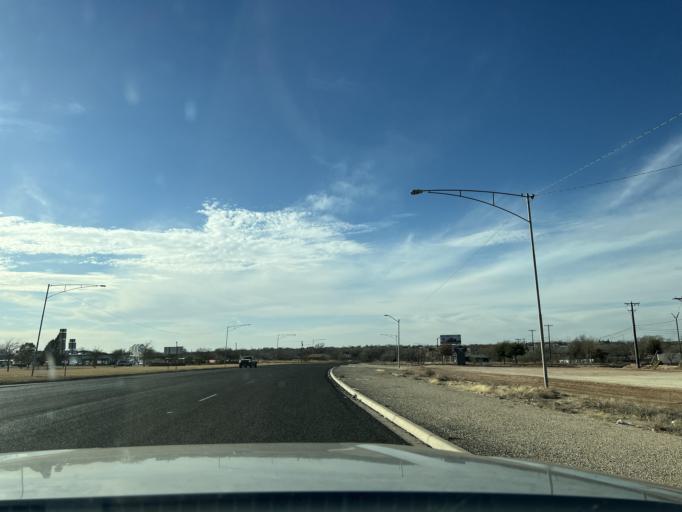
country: US
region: Texas
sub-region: Scurry County
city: Snyder
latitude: 32.7022
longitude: -100.8783
